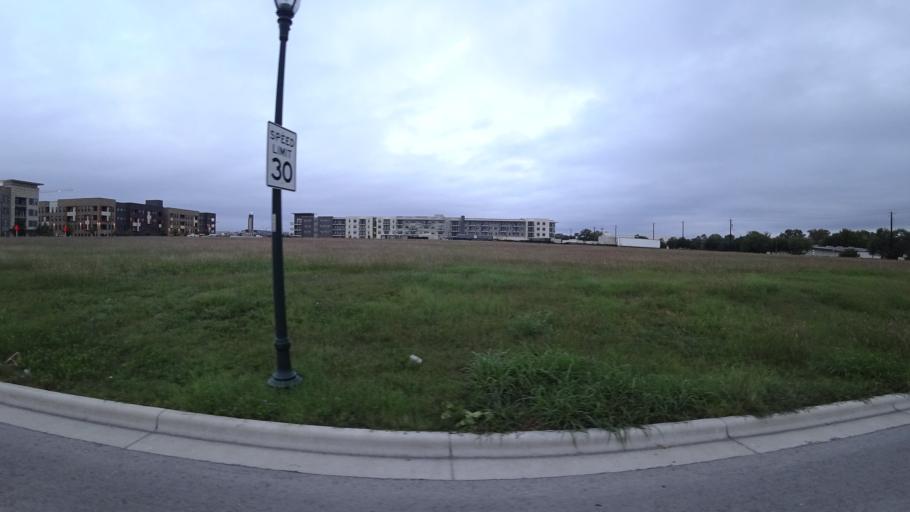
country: US
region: Texas
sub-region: Travis County
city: Austin
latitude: 30.3032
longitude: -97.6995
